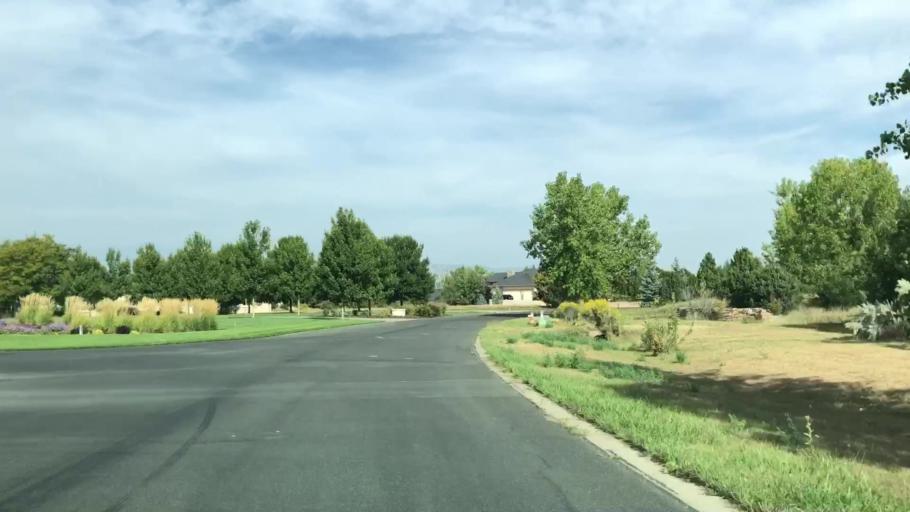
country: US
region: Colorado
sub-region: Larimer County
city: Loveland
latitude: 40.4375
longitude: -105.0541
